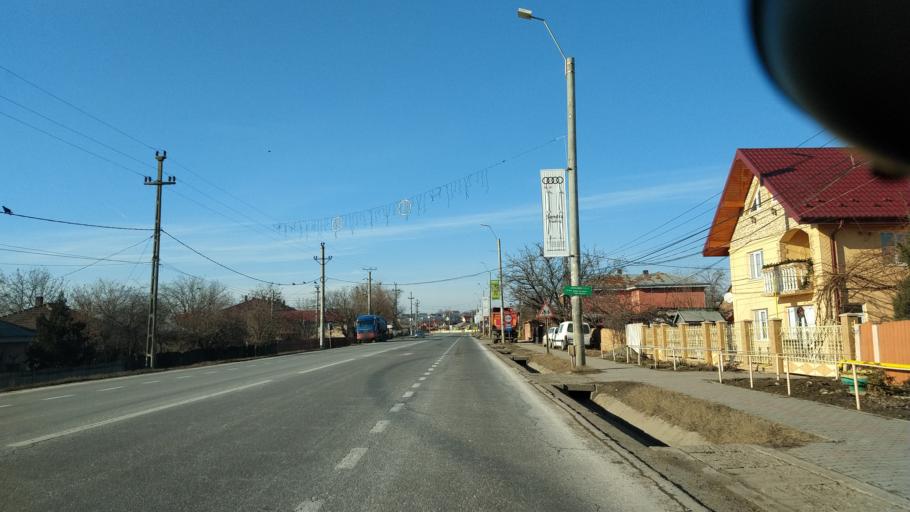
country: RO
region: Iasi
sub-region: Comuna Letcani
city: Letcani
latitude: 47.1939
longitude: 27.4198
